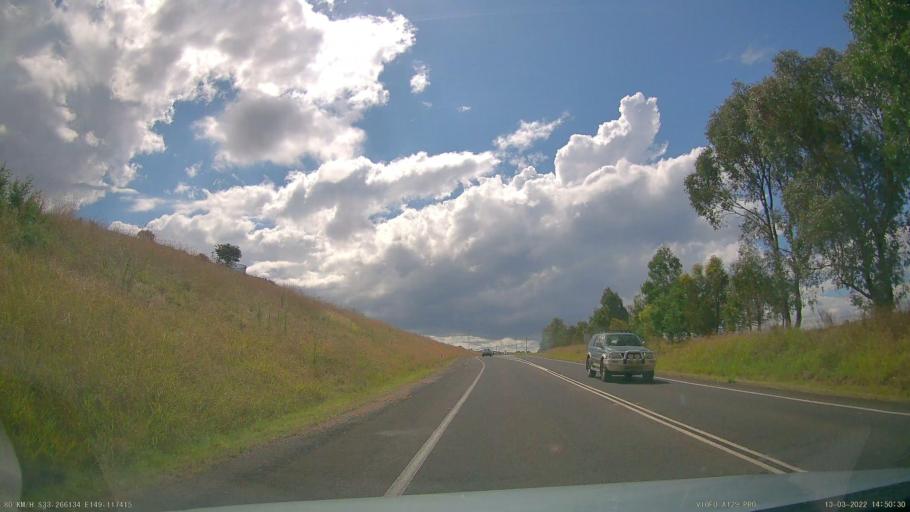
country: AU
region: New South Wales
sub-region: Orange Municipality
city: Orange
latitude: -33.2659
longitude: 149.1173
